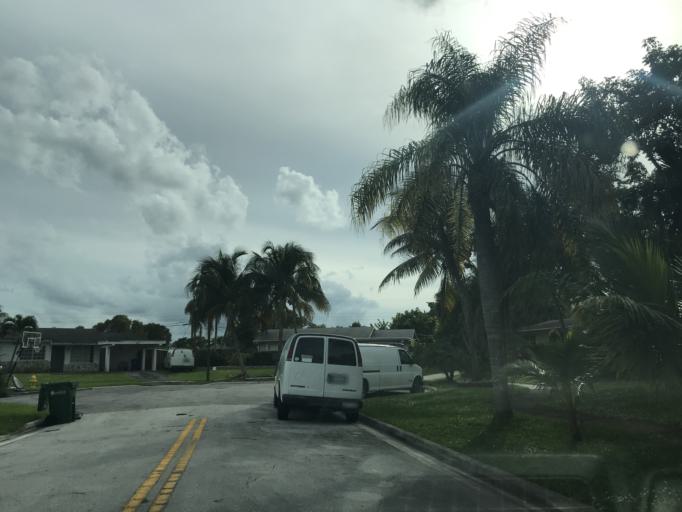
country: US
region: Florida
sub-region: Broward County
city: Margate
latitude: 26.2566
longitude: -80.2064
